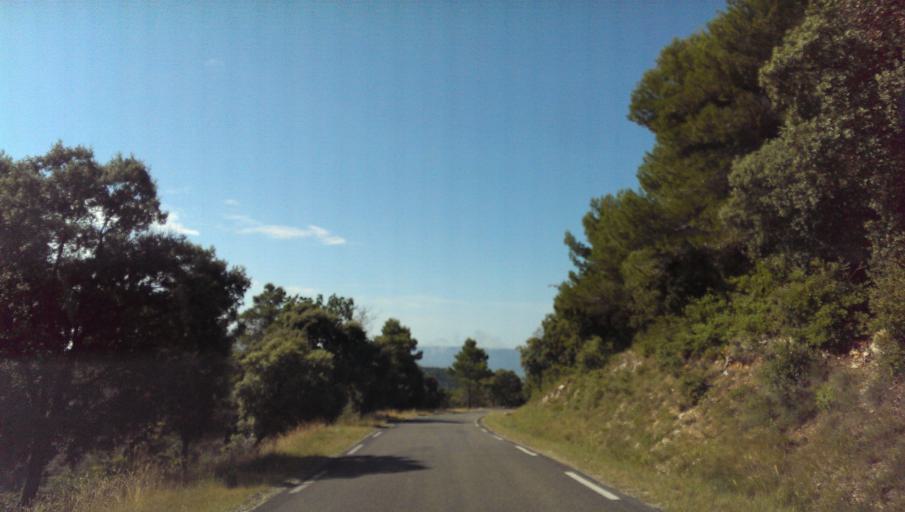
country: FR
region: Provence-Alpes-Cote d'Azur
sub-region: Departement du Vaucluse
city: Gordes
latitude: 43.9478
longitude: 5.1952
